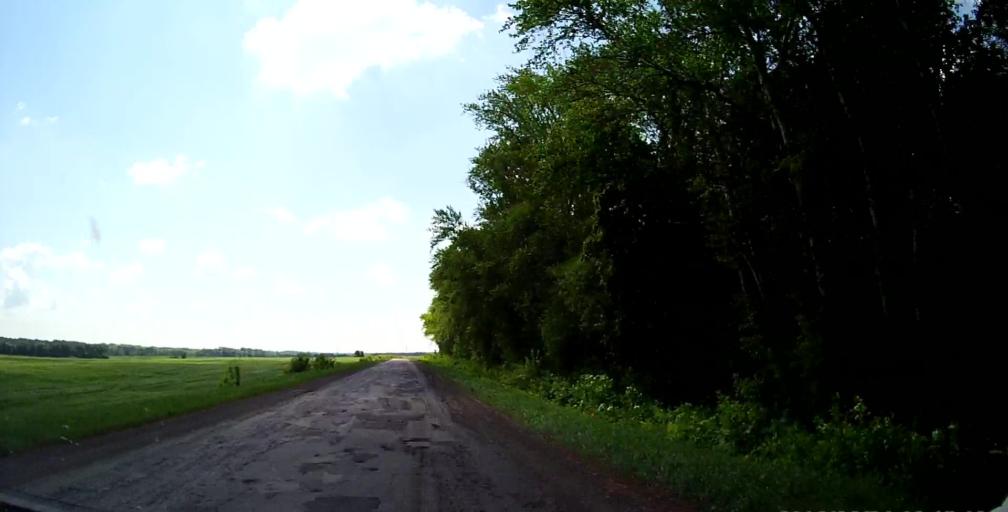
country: RU
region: Lipetsk
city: Chaplygin
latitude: 53.2996
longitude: 39.9527
